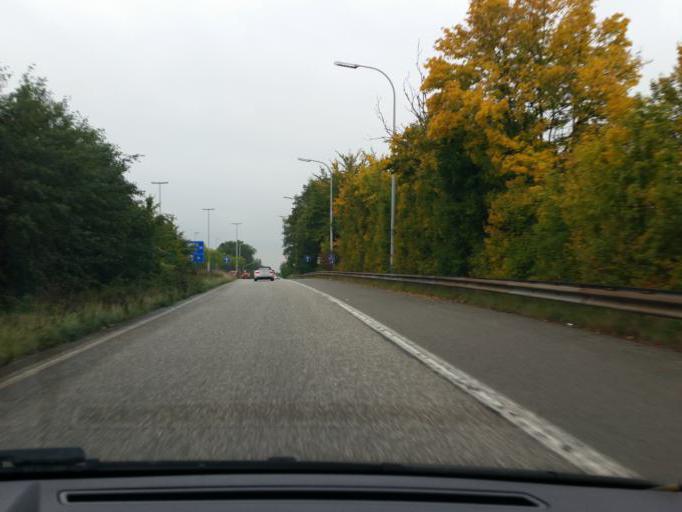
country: BE
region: Flanders
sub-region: Provincie Antwerpen
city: Edegem
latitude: 51.1731
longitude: 4.4097
